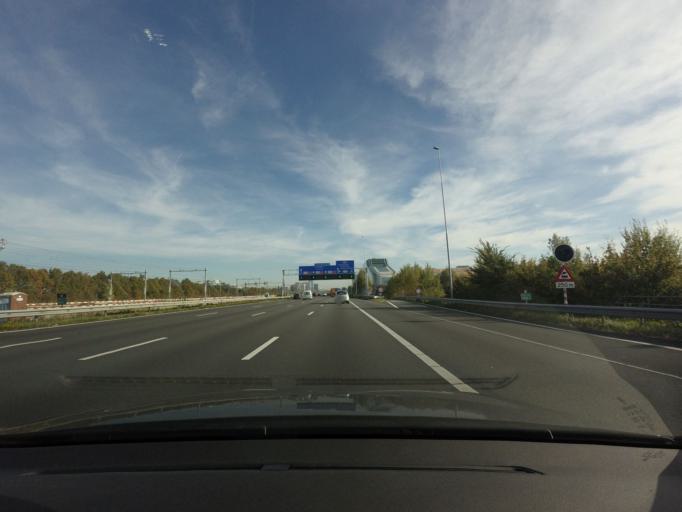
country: NL
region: North Holland
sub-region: Gemeente Amstelveen
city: Amstelveen
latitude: 52.3373
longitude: 4.8502
